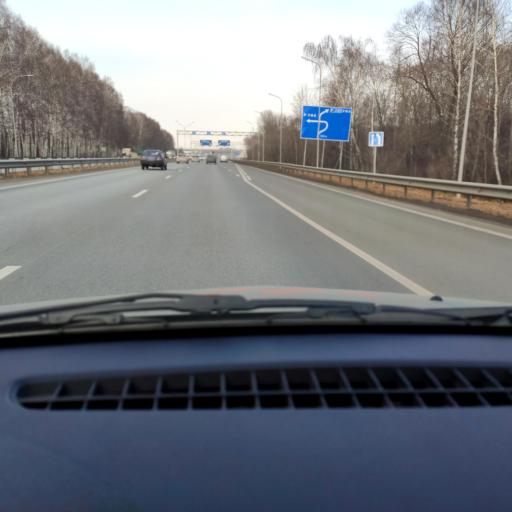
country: RU
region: Bashkortostan
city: Ufa
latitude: 54.5688
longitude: 55.9168
